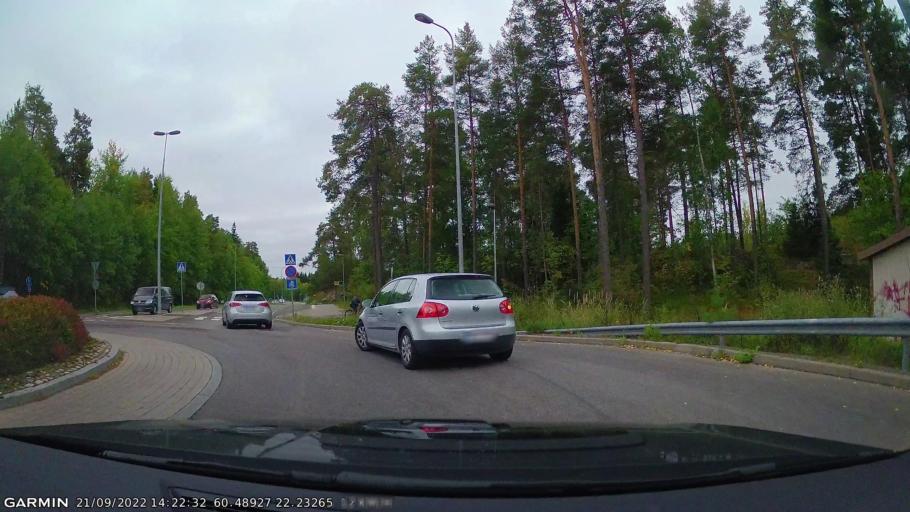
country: FI
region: Varsinais-Suomi
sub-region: Turku
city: Rusko
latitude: 60.4890
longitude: 22.2324
